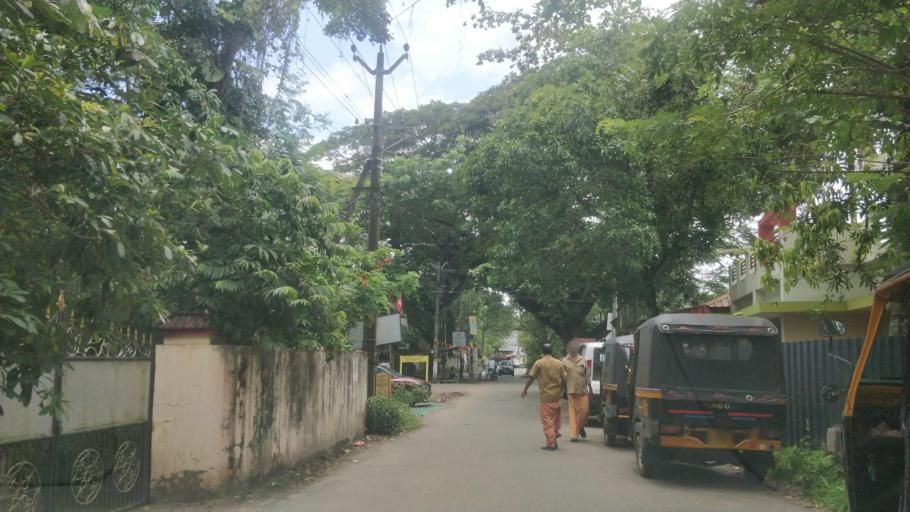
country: IN
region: Kerala
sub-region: Alappuzha
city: Shertallai
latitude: 9.6636
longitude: 76.3823
